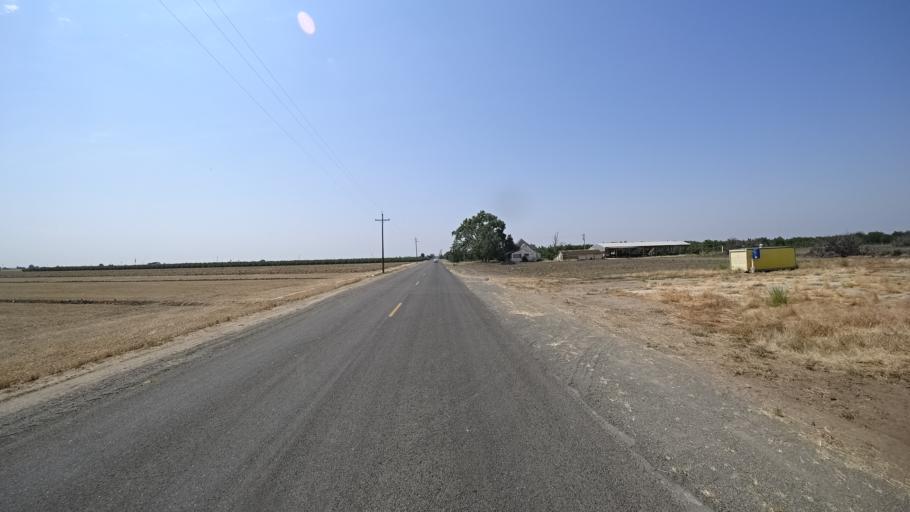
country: US
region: California
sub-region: Fresno County
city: Laton
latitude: 36.3949
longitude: -119.7450
